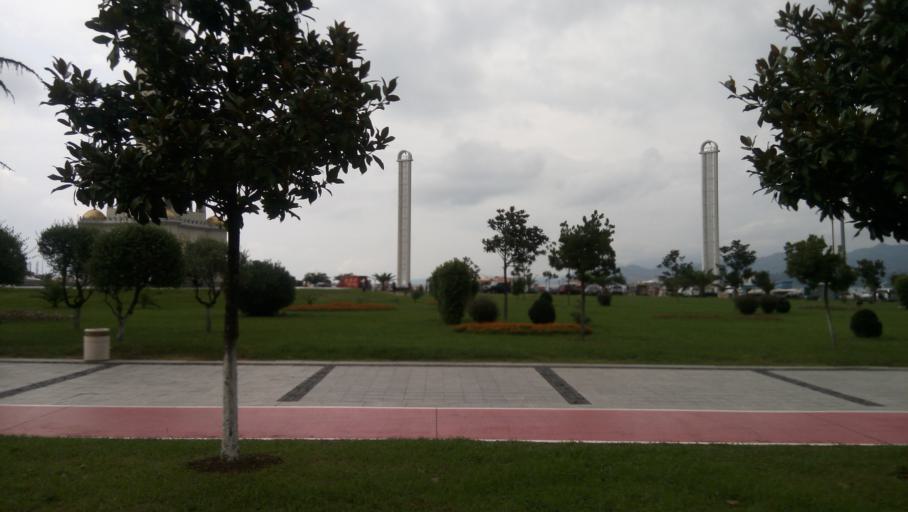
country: GE
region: Ajaria
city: Batumi
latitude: 41.6521
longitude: 41.6426
